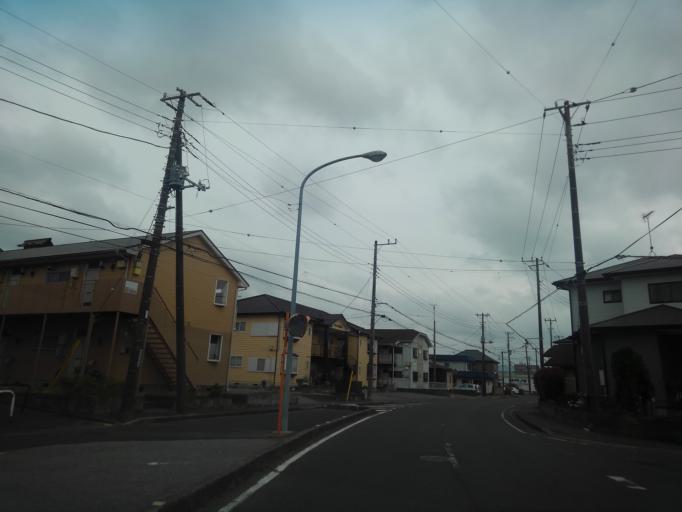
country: JP
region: Chiba
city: Kimitsu
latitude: 35.3273
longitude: 139.9235
